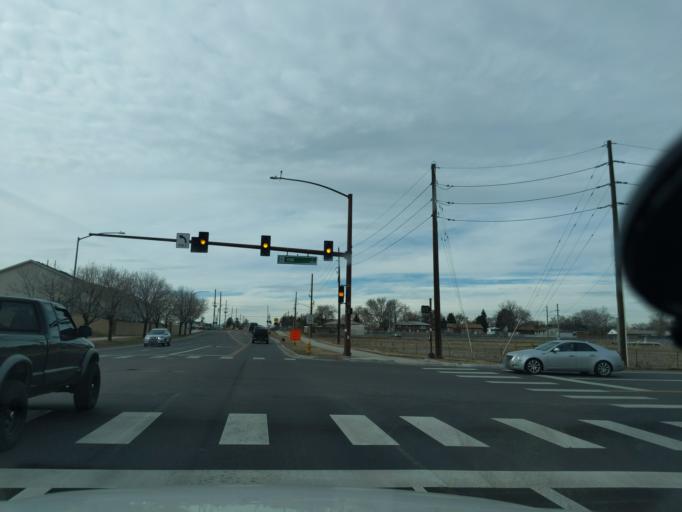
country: US
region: Colorado
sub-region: Adams County
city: Northglenn
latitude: 39.8995
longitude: -104.9586
